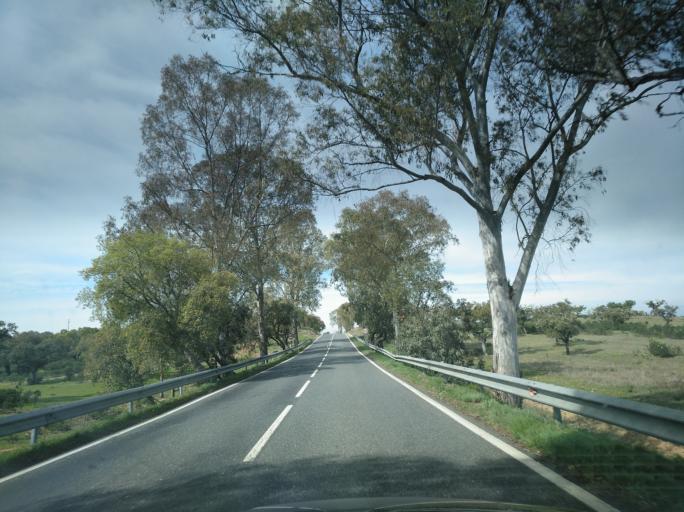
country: PT
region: Beja
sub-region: Mertola
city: Mertola
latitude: 37.7348
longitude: -7.7720
